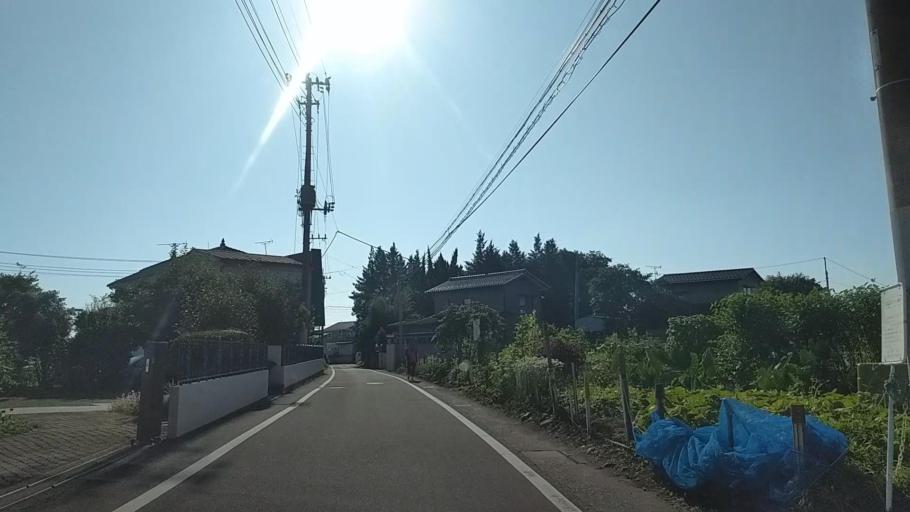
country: JP
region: Gunma
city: Annaka
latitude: 36.3256
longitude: 138.8860
